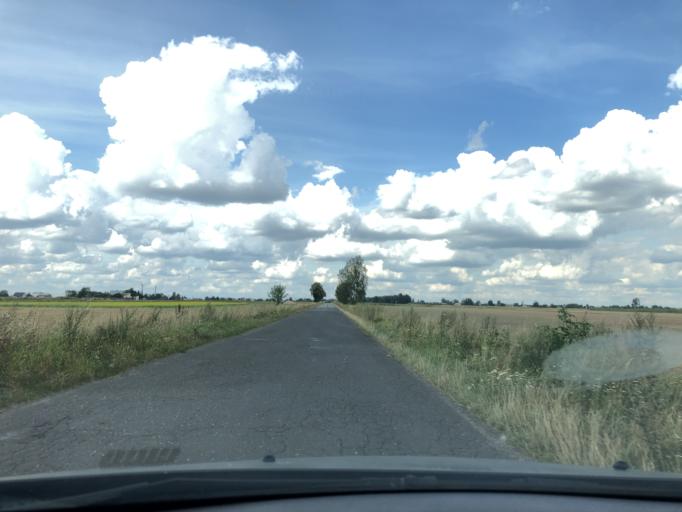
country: PL
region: Lodz Voivodeship
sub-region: Powiat wieruszowski
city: Walichnowy
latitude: 51.2493
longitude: 18.3896
